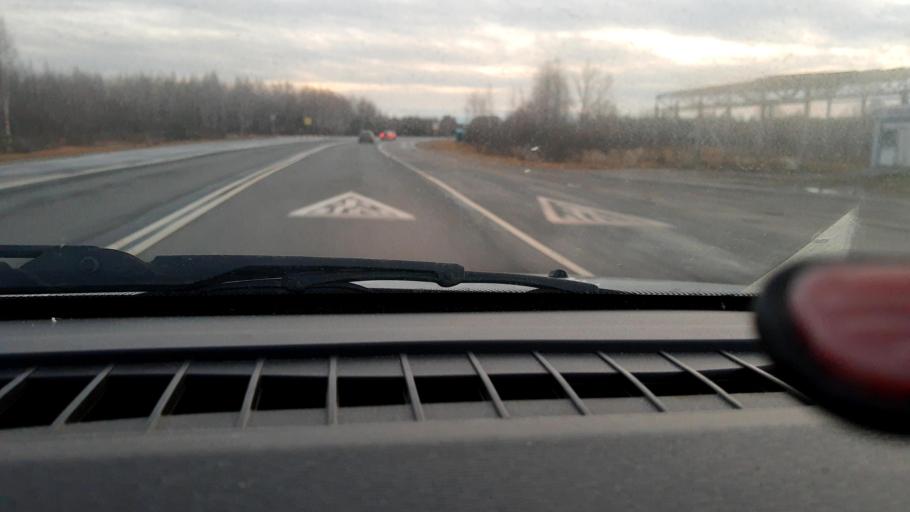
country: RU
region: Nizjnij Novgorod
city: Krasnyye Baki
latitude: 57.0863
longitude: 45.1476
